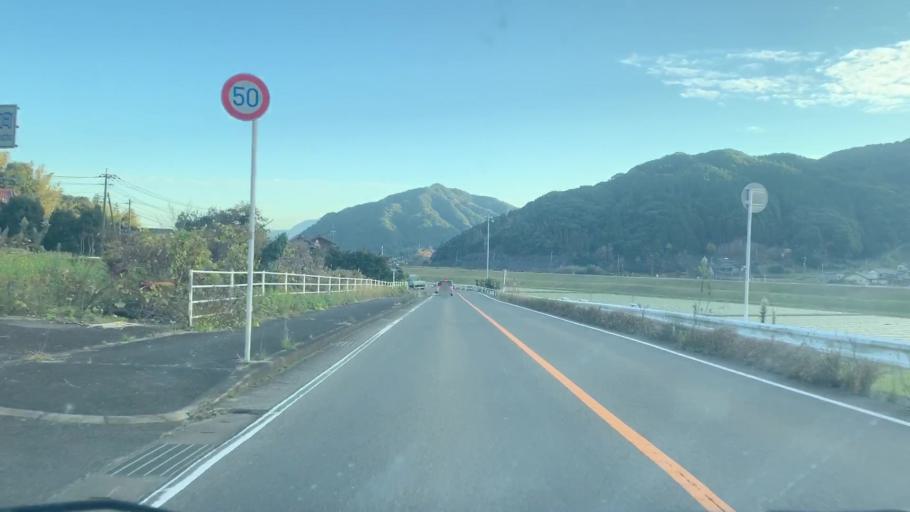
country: JP
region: Saga Prefecture
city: Karatsu
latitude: 33.3828
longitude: 129.9893
